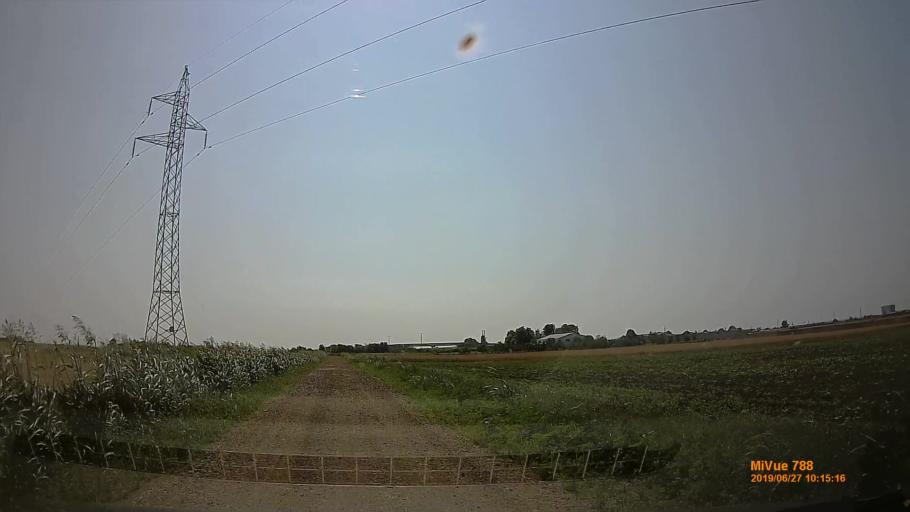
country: HU
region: Pest
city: Cegled
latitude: 47.1971
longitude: 19.8216
